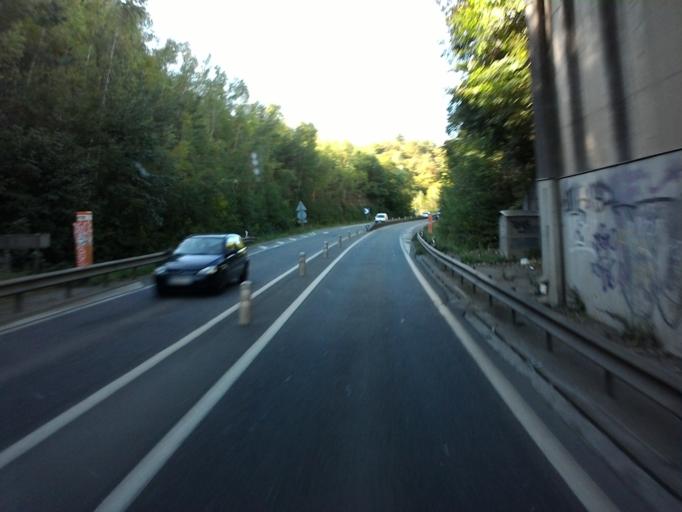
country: FR
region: Lorraine
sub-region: Departement de Meurthe-et-Moselle
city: Rehon
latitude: 49.5076
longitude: 5.7530
